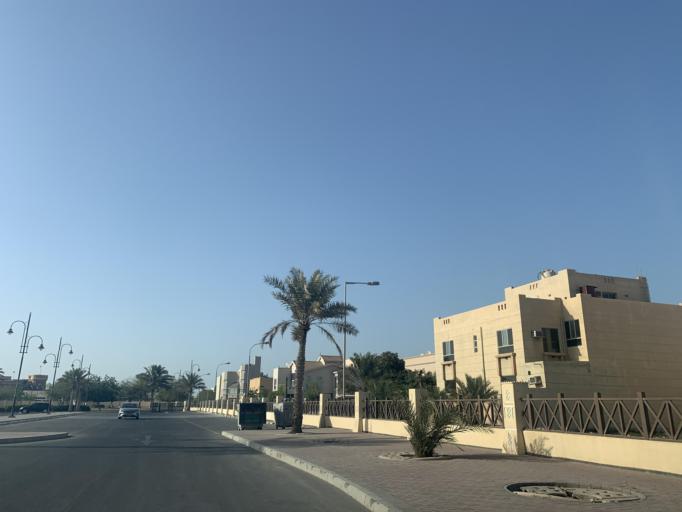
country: BH
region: Manama
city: Jidd Hafs
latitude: 26.2079
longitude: 50.4471
